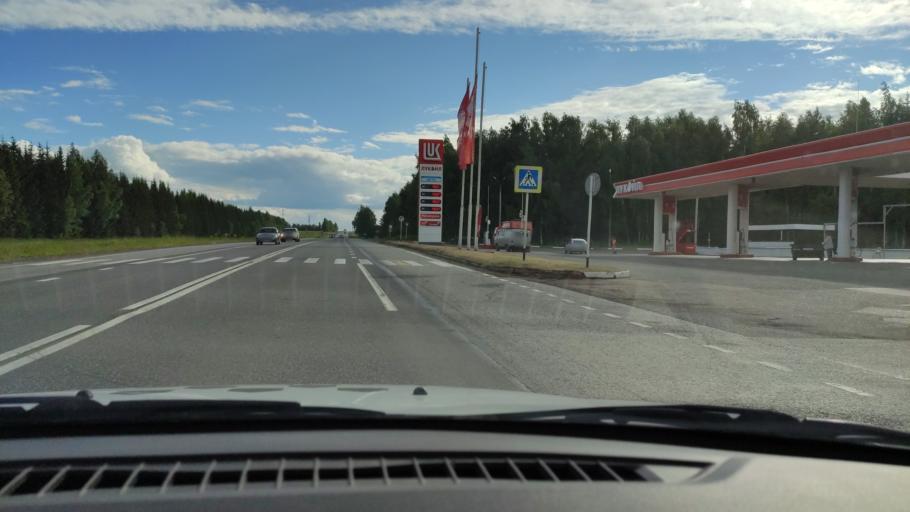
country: RU
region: Perm
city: Kungur
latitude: 57.4101
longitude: 56.9064
